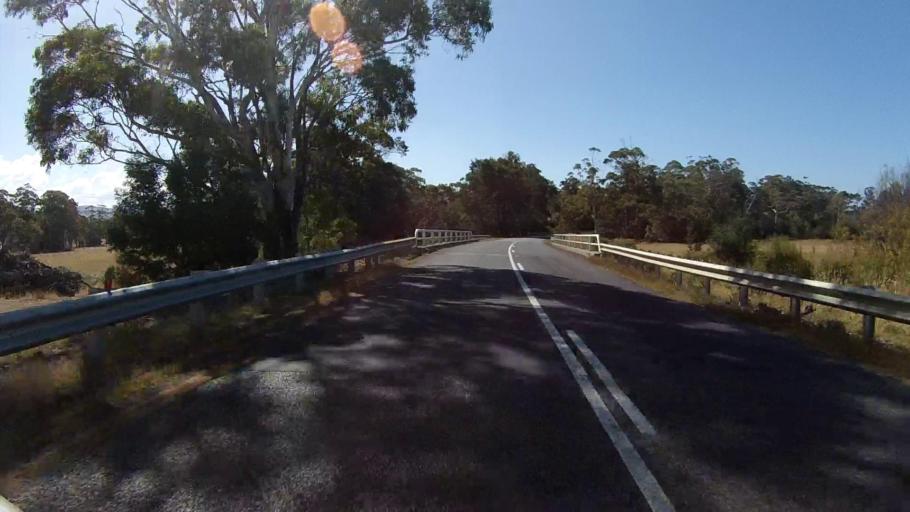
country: AU
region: Tasmania
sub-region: Sorell
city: Sorell
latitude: -42.2629
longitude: 148.0021
